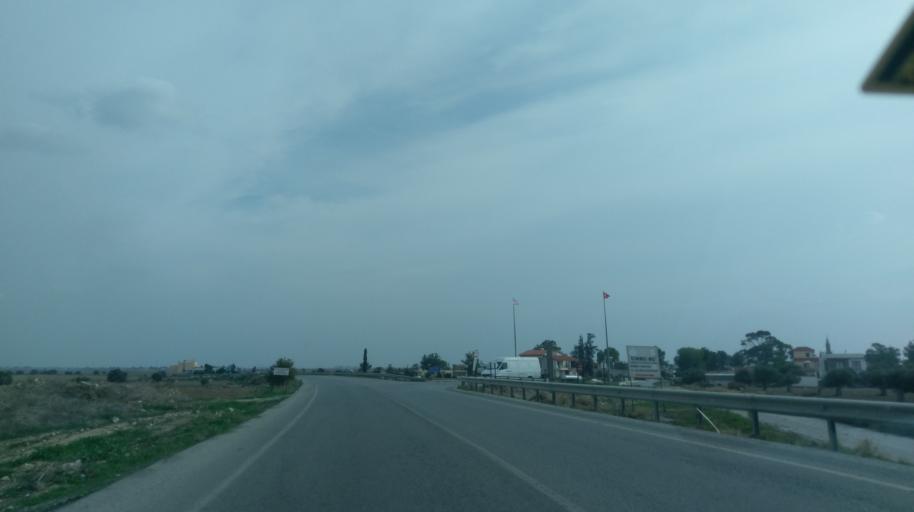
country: CY
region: Ammochostos
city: Lefkonoiko
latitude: 35.2572
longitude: 33.6825
